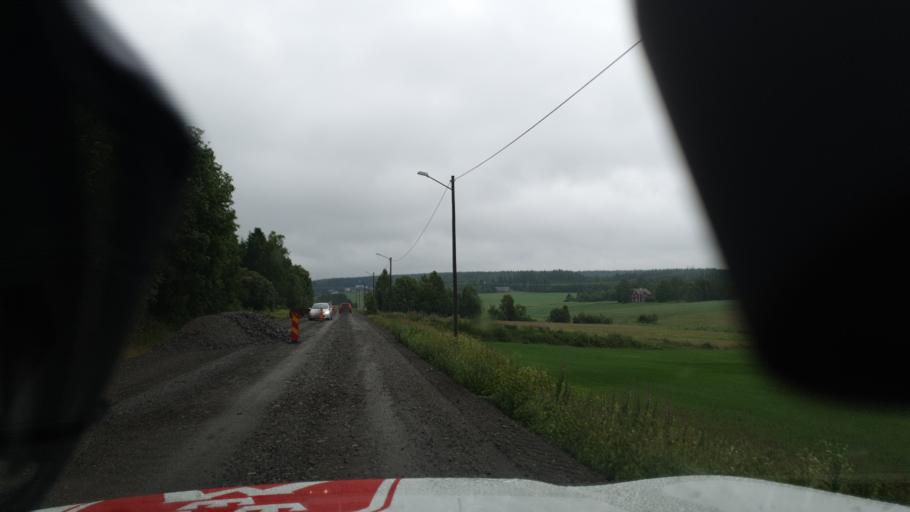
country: SE
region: Vaesterbotten
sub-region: Vannas Kommun
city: Vaennaes
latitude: 63.7377
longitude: 19.6531
